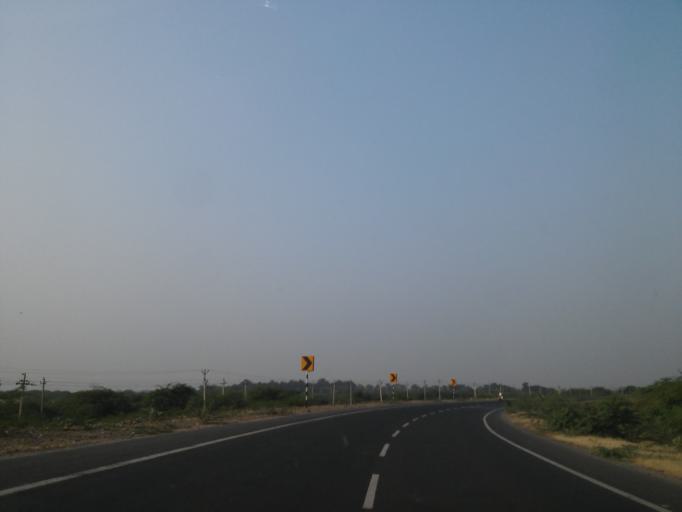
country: IN
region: Gujarat
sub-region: Kachchh
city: Bhachau
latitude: 23.3128
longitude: 70.1355
